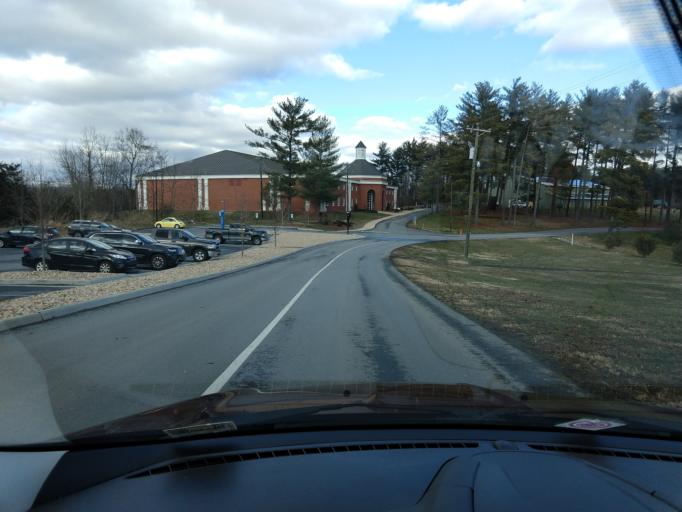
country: US
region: Virginia
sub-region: City of Lexington
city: Lexington
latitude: 37.7932
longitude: -79.4455
